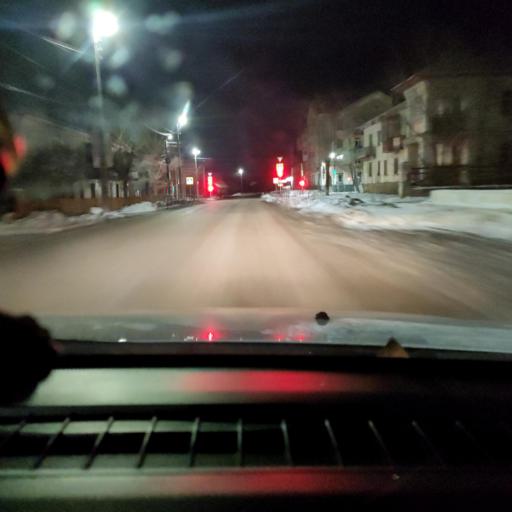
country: RU
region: Samara
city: Novokuybyshevsk
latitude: 53.1023
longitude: 49.9489
